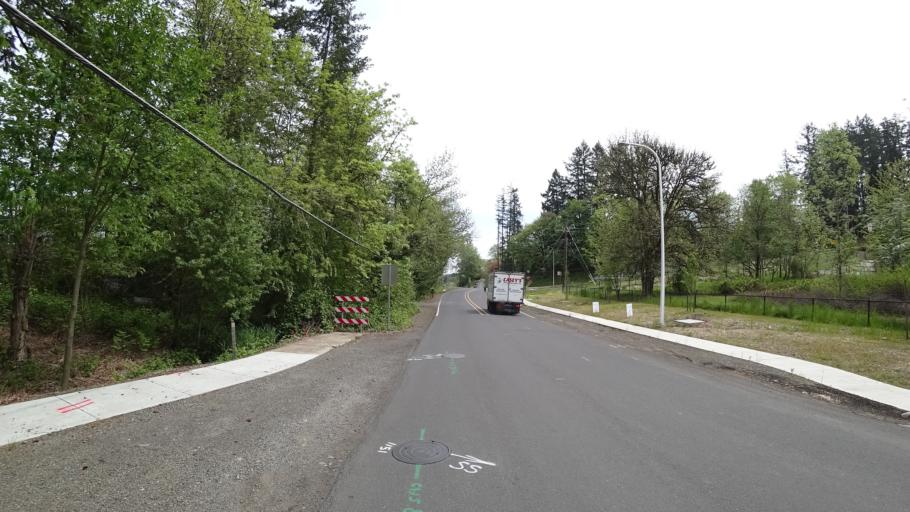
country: US
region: Oregon
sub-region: Washington County
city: Aloha
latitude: 45.4620
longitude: -122.8578
